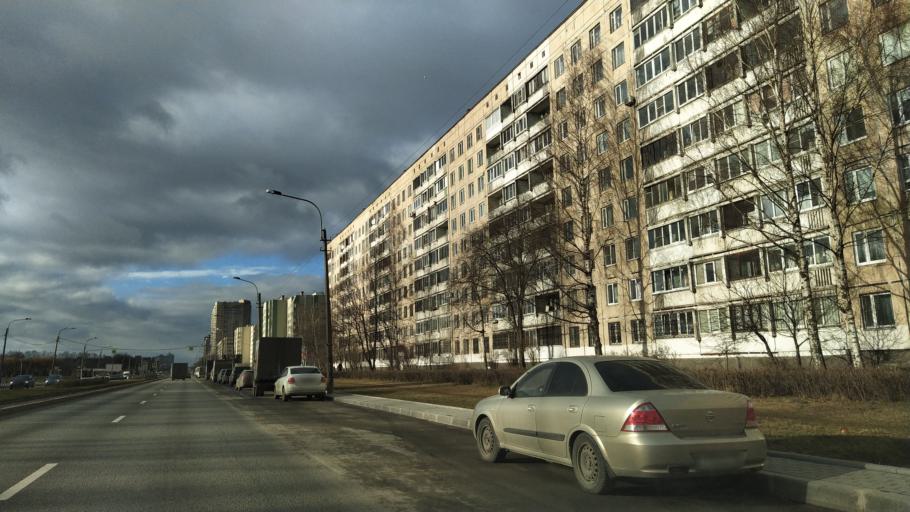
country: RU
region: St.-Petersburg
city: Grazhdanka
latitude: 60.0318
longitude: 30.3881
